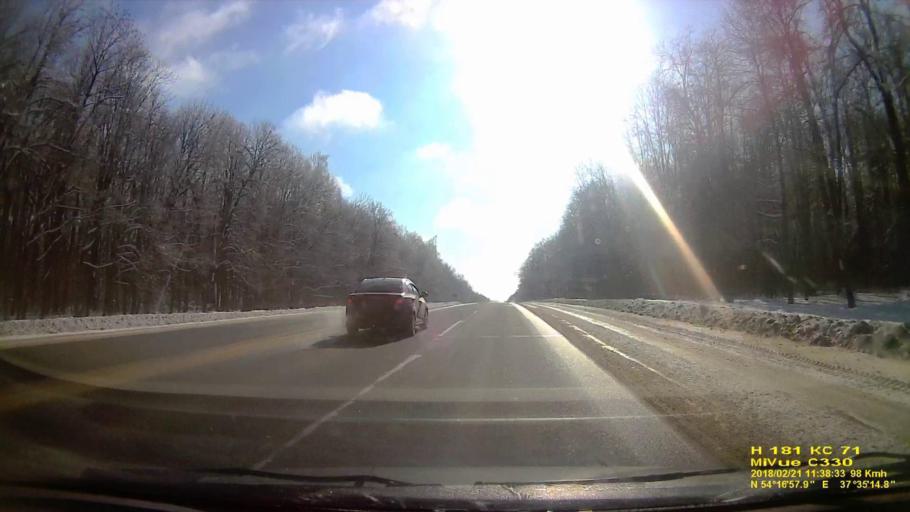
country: RU
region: Tula
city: Gorelki
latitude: 54.2826
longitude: 37.5876
